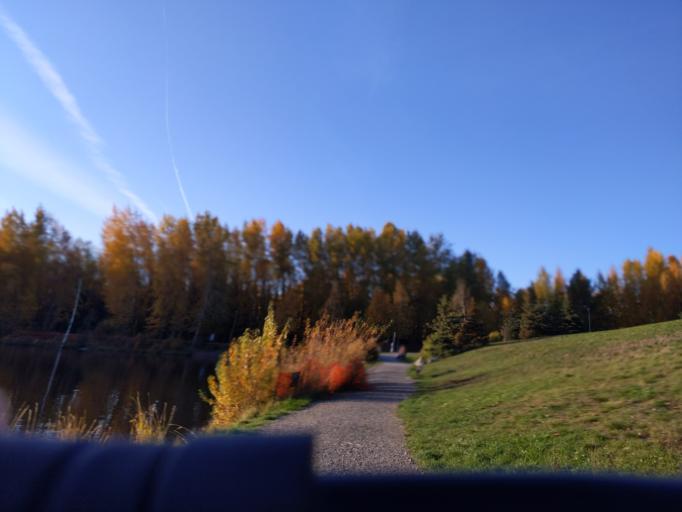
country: US
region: Alaska
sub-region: Anchorage Municipality
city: Anchorage
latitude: 61.1510
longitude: -149.8796
